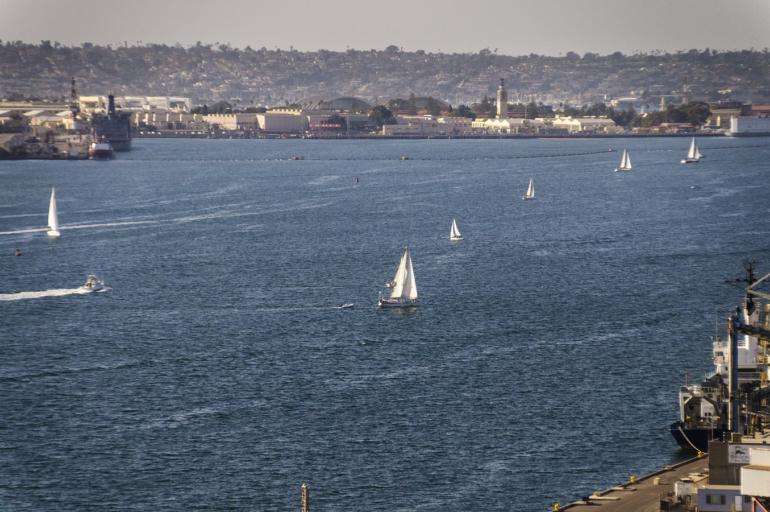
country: US
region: California
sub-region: San Diego County
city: San Diego
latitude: 32.6943
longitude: -117.1489
